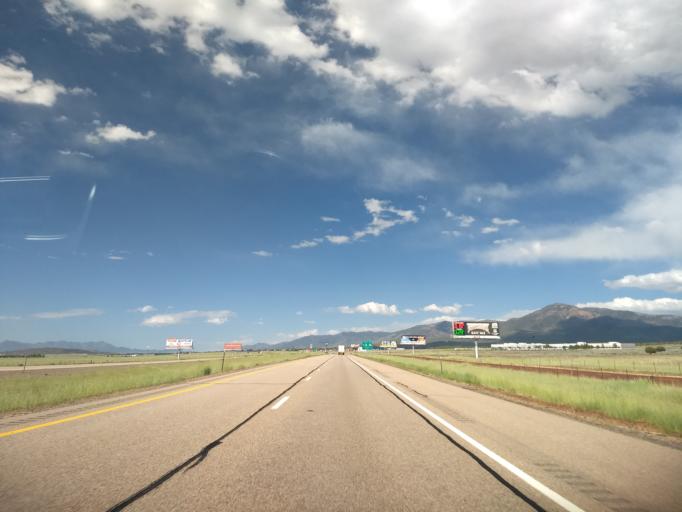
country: US
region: Utah
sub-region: Millard County
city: Fillmore
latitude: 38.9359
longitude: -112.3604
